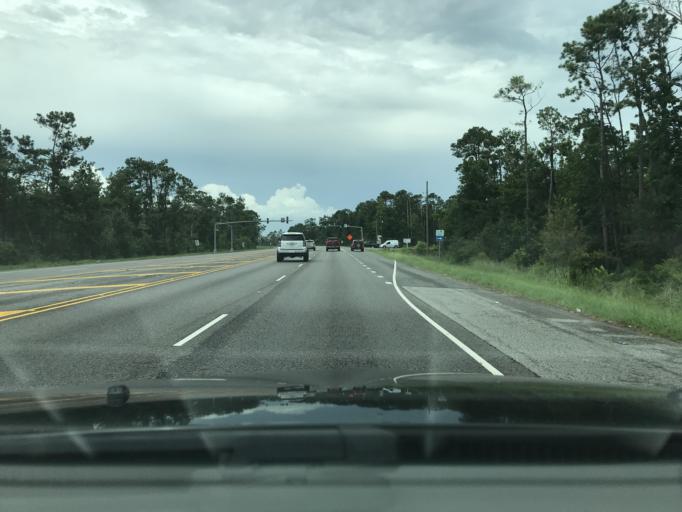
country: US
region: Louisiana
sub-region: Calcasieu Parish
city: Moss Bluff
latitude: 30.2753
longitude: -93.1830
